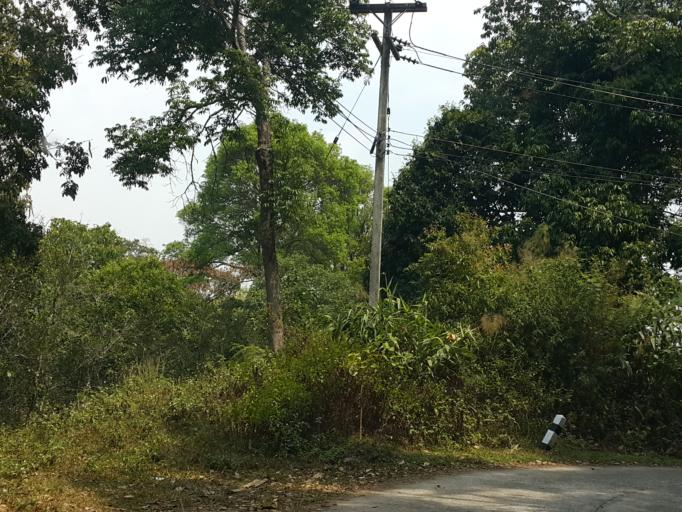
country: TH
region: Lampang
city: Mueang Pan
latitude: 18.8260
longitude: 99.4104
